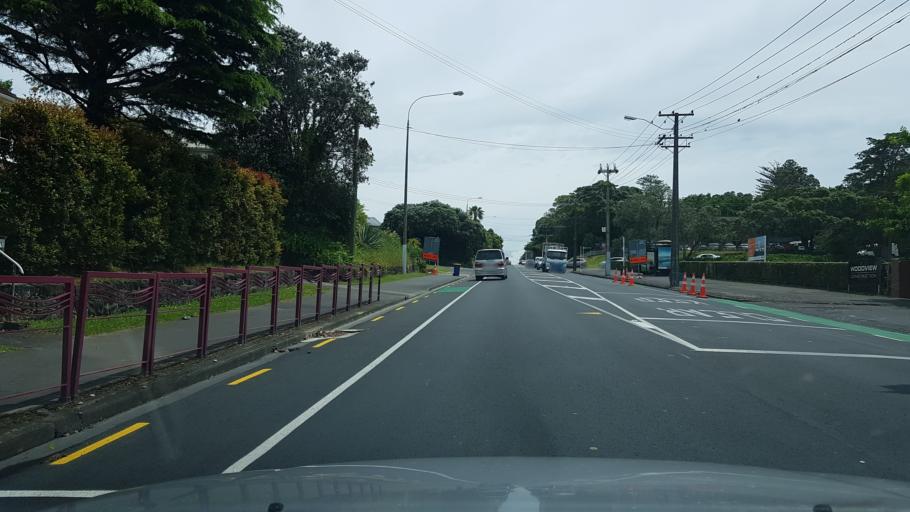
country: NZ
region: Auckland
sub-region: Auckland
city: North Shore
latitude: -36.8016
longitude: 174.7870
